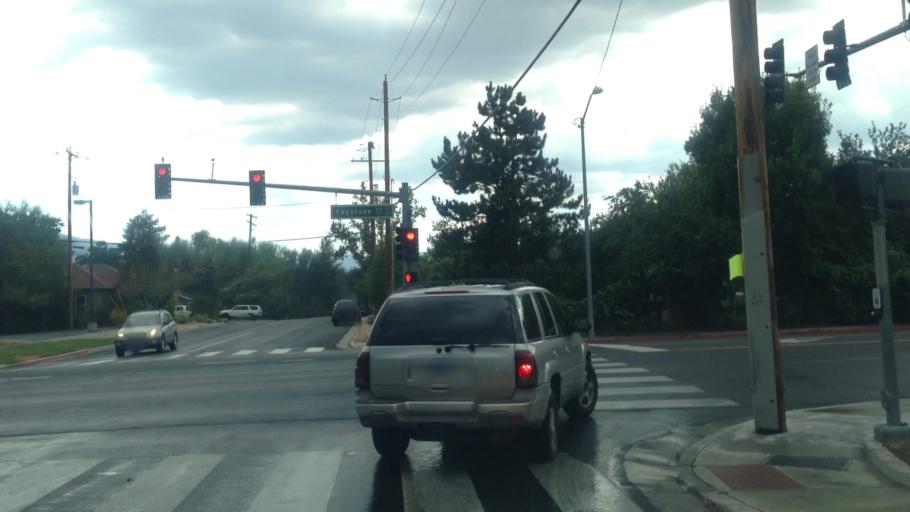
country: US
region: Nevada
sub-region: Washoe County
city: Reno
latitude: 39.5234
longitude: -119.8251
